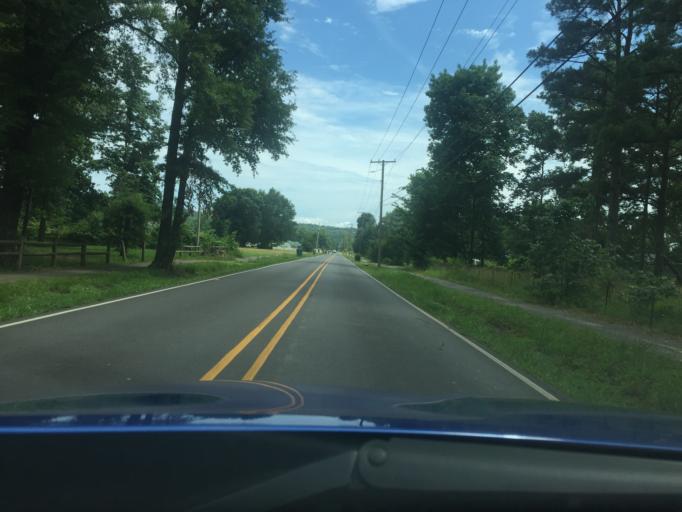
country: US
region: Arkansas
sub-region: Pulaski County
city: Maumelle
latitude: 34.8286
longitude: -92.4358
